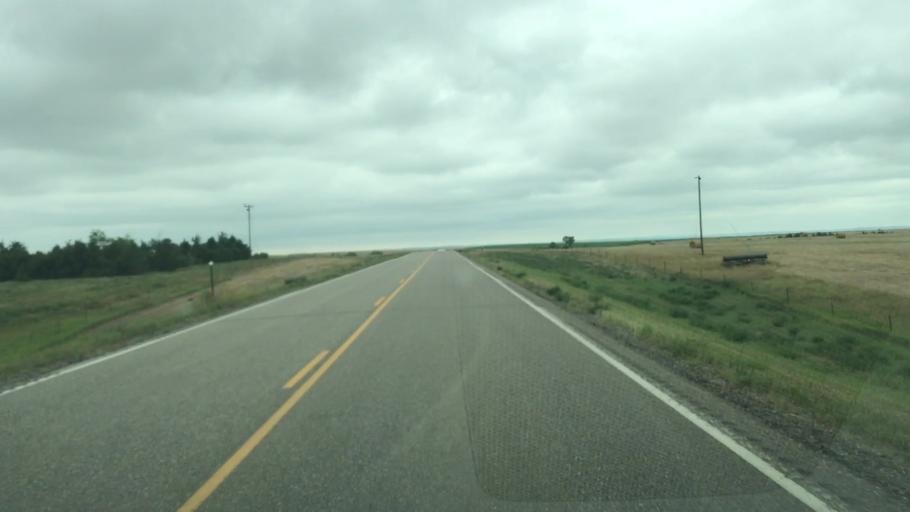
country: US
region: South Dakota
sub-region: Jackson County
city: Kadoka
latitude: 43.8212
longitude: -101.5224
